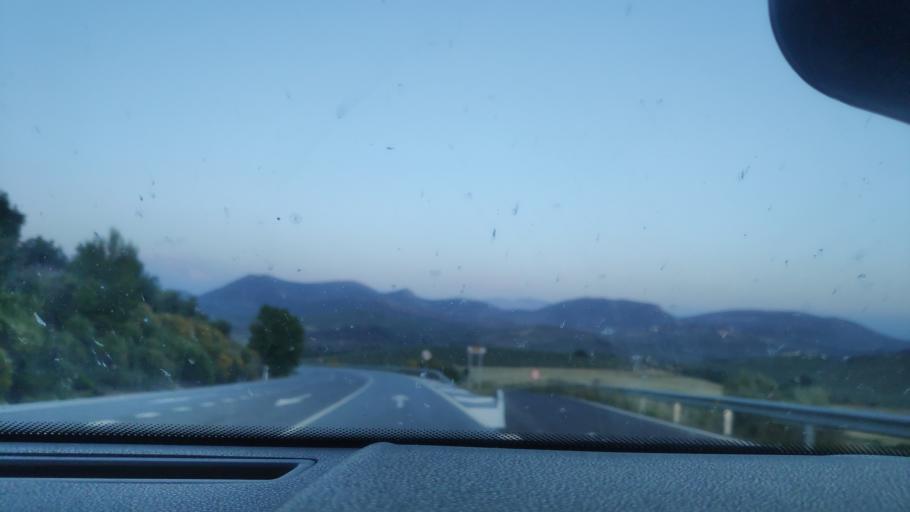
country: ES
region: Andalusia
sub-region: Provincia de Granada
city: Benalua de las Villas
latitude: 37.4281
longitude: -3.7494
